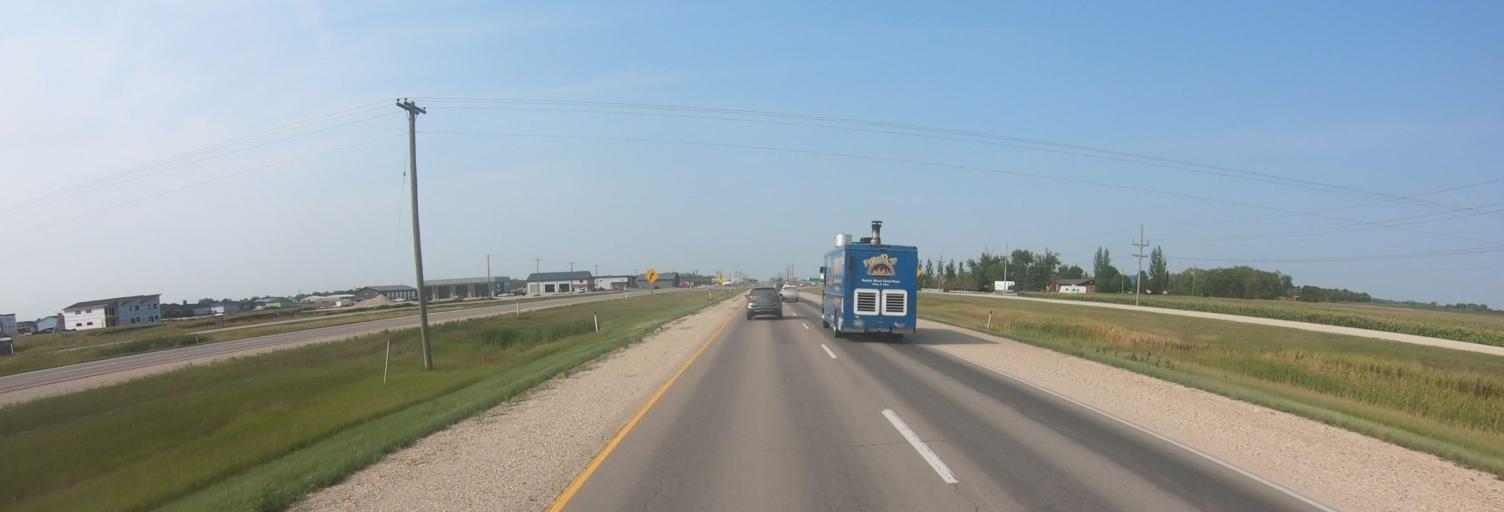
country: CA
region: Manitoba
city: Steinbach
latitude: 49.5928
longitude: -96.6877
